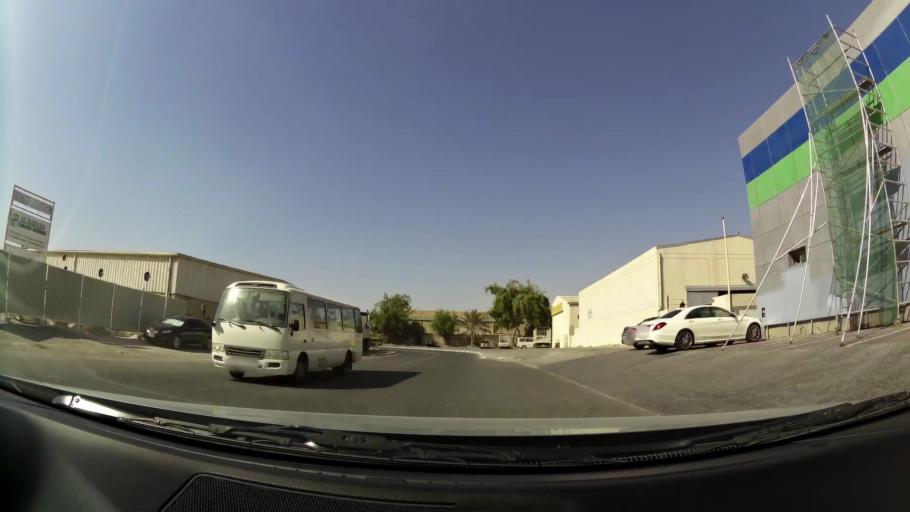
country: AE
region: Dubai
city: Dubai
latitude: 25.1190
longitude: 55.2213
